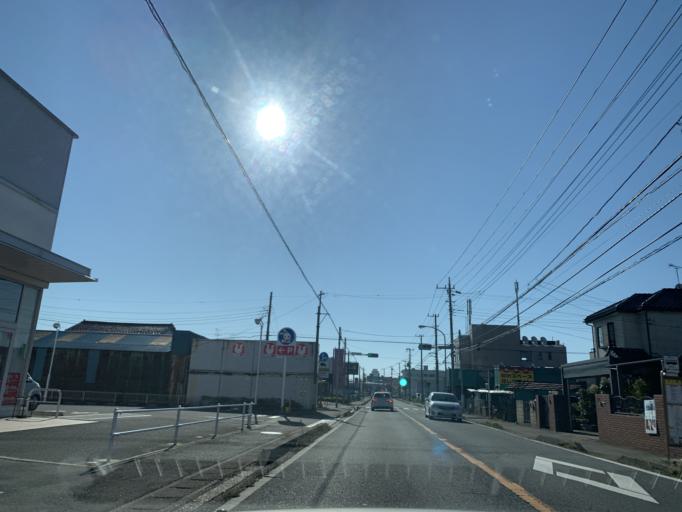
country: JP
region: Chiba
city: Matsudo
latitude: 35.7985
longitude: 139.8963
